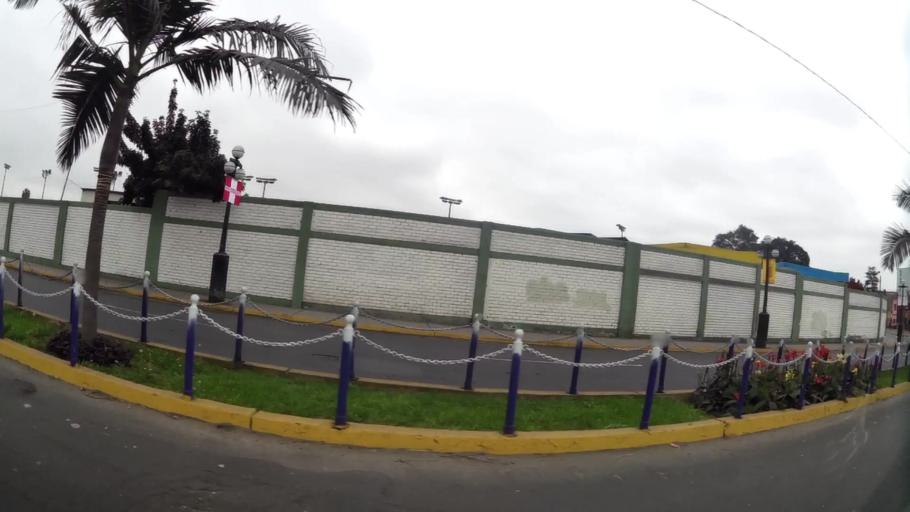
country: PE
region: Lima
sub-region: Lima
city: Surco
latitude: -12.1619
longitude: -77.0234
